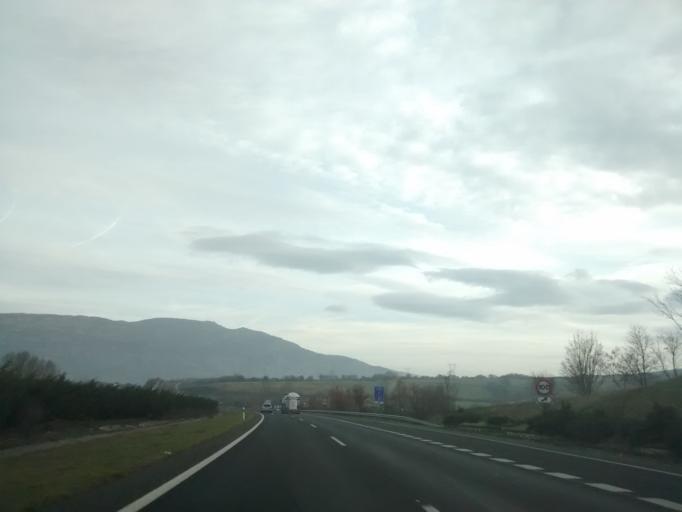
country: ES
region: Navarre
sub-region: Provincia de Navarra
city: Arbizu
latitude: 42.9078
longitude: -2.0419
